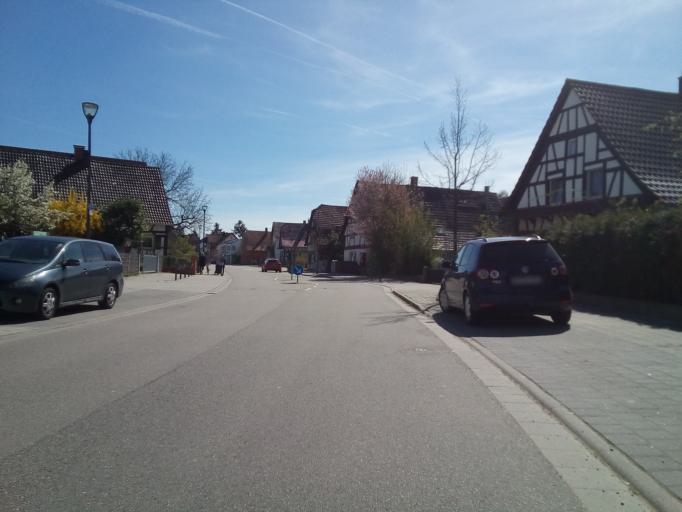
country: DE
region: Baden-Wuerttemberg
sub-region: Freiburg Region
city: Rheinau
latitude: 48.6670
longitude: 7.9354
